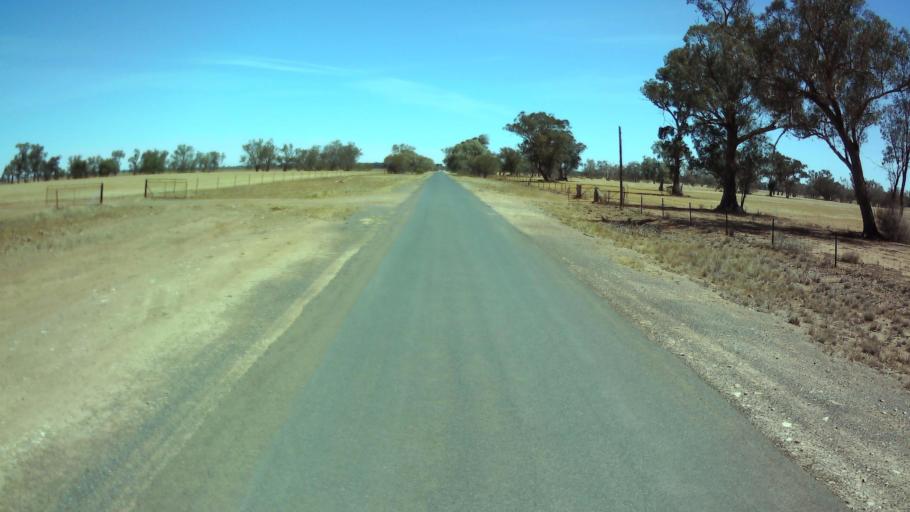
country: AU
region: New South Wales
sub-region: Weddin
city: Grenfell
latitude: -33.8456
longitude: 147.6965
